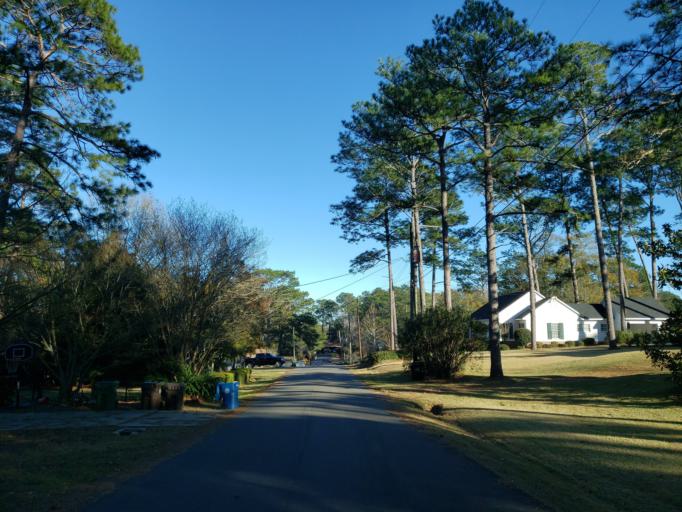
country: US
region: Mississippi
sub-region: Forrest County
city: Hattiesburg
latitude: 31.3147
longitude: -89.3163
